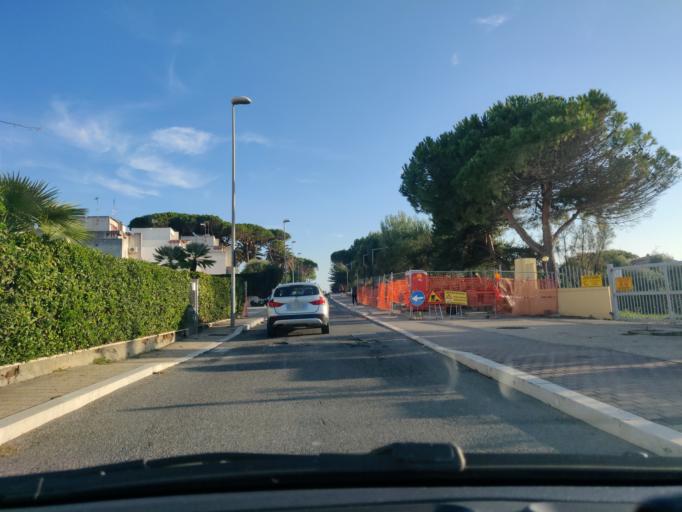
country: IT
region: Latium
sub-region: Citta metropolitana di Roma Capitale
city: Santa Marinella
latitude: 42.0336
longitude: 11.8336
